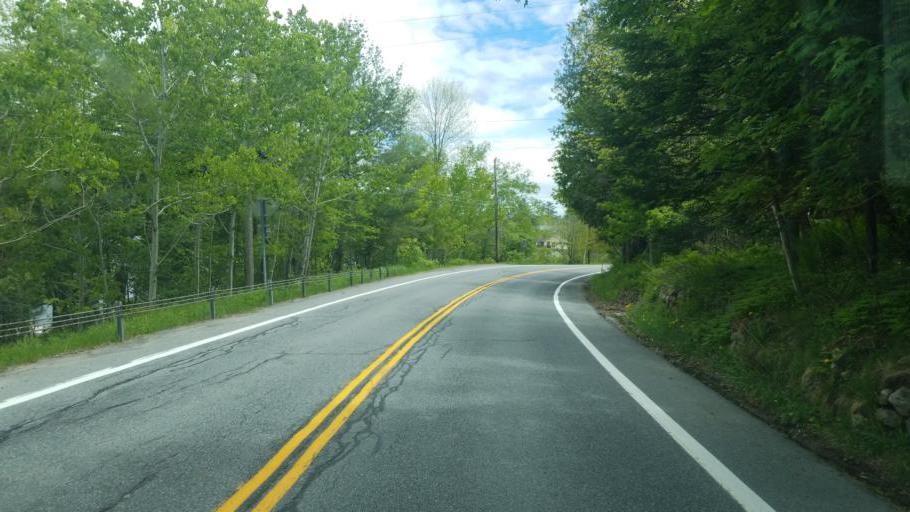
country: US
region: New York
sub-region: Franklin County
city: Tupper Lake
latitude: 43.8551
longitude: -74.4410
